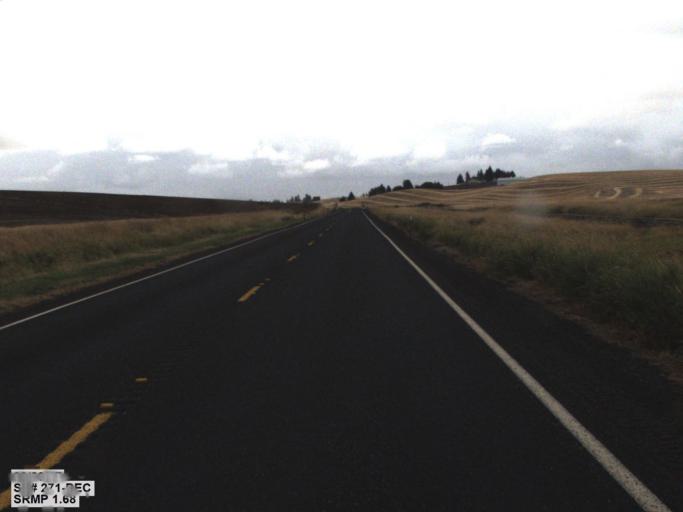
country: US
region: Washington
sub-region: Whitman County
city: Colfax
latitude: 47.1544
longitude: -117.2629
